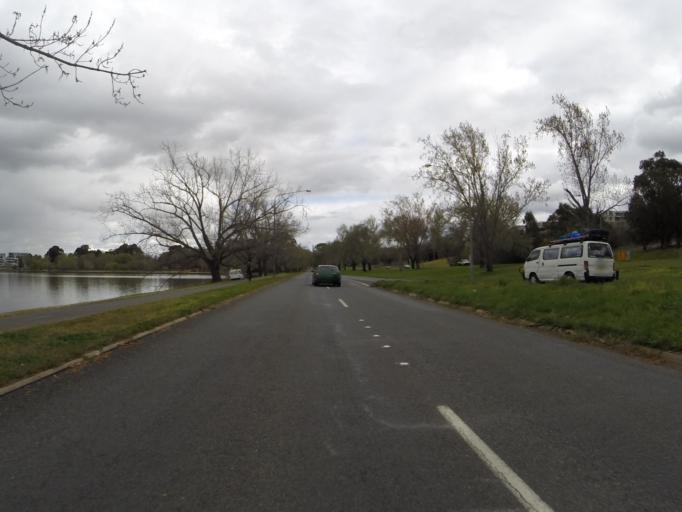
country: AU
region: Australian Capital Territory
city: Forrest
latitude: -35.3053
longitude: 149.1402
